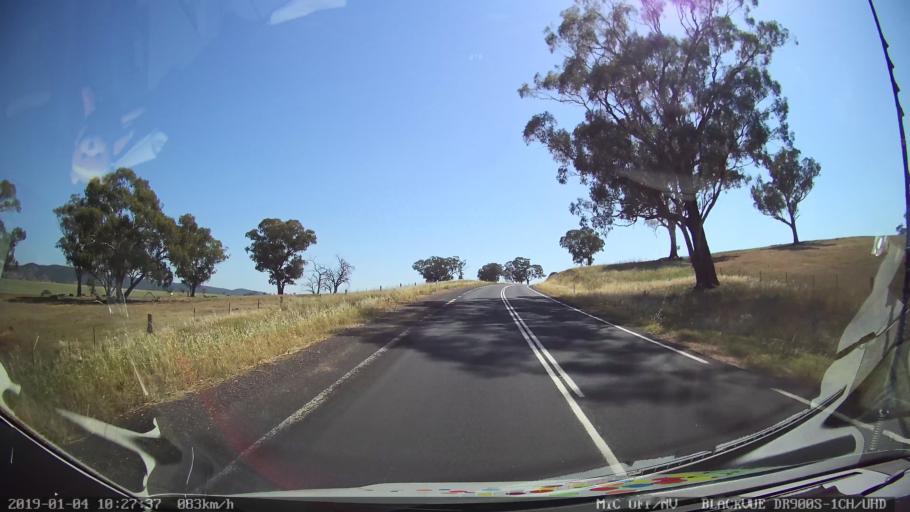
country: AU
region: New South Wales
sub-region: Cabonne
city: Canowindra
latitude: -33.3683
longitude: 148.6001
